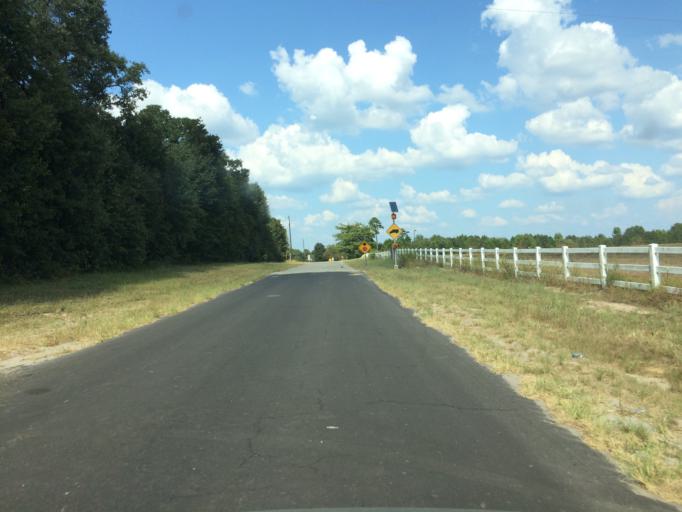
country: US
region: Texas
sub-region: Wood County
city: Hawkins
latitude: 32.6658
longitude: -95.2044
